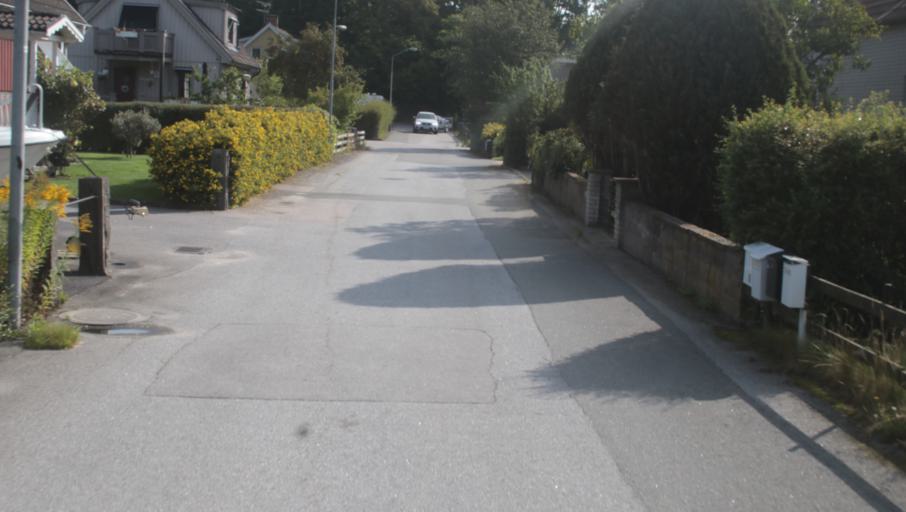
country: SE
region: Blekinge
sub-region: Karlshamns Kommun
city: Karlshamn
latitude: 56.1906
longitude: 14.8529
